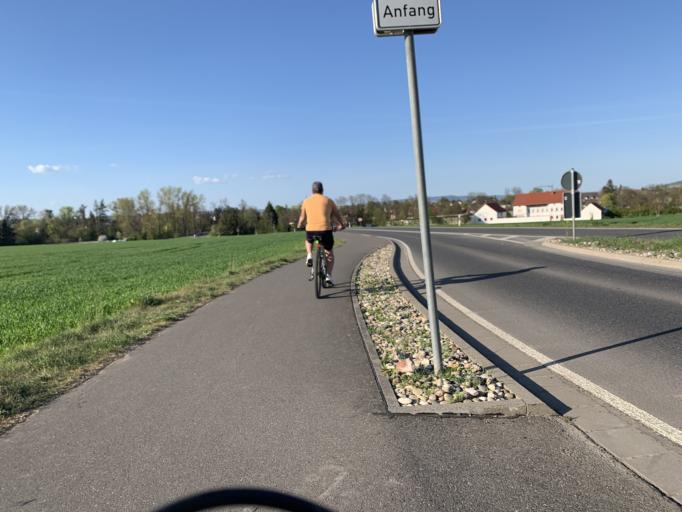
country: DE
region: Rheinland-Pfalz
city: Bretzenheim
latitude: 49.8831
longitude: 7.8988
